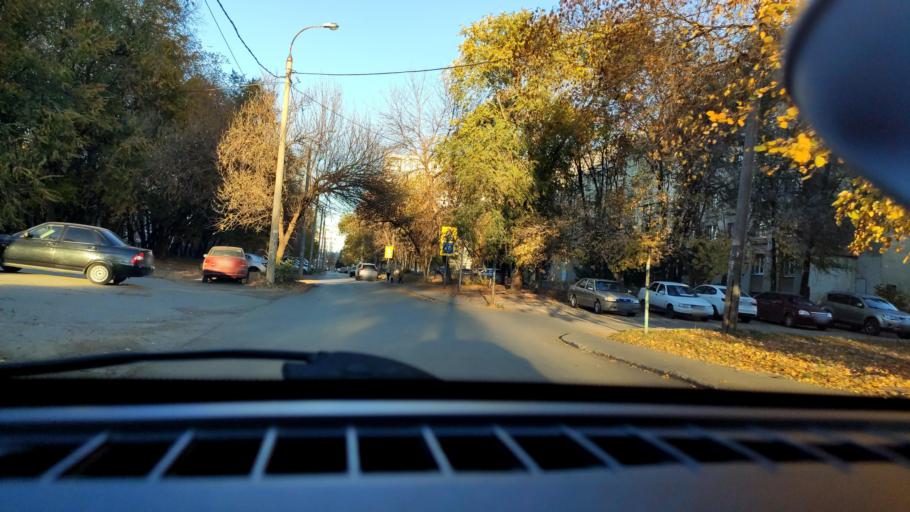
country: RU
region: Samara
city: Samara
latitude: 53.2373
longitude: 50.2093
